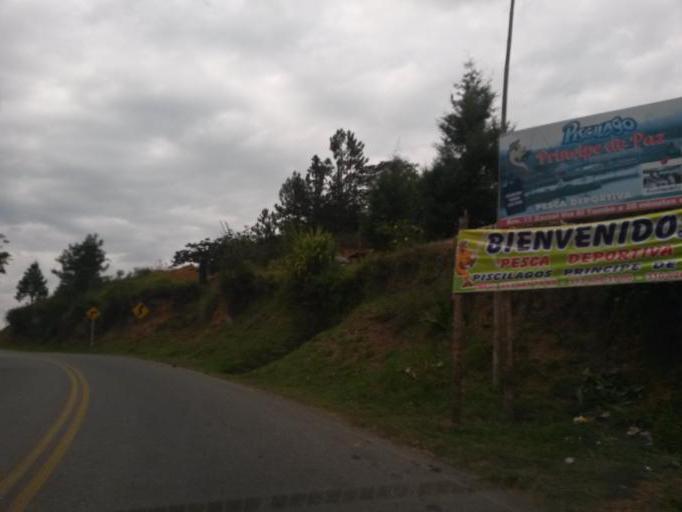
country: CO
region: Cauca
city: Lopez
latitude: 2.4480
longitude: -76.7387
